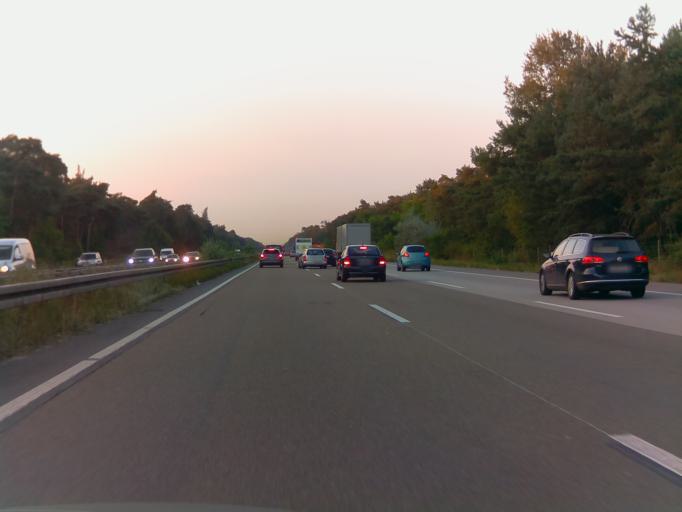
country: DE
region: Hesse
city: Lorsch
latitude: 49.6085
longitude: 8.5583
